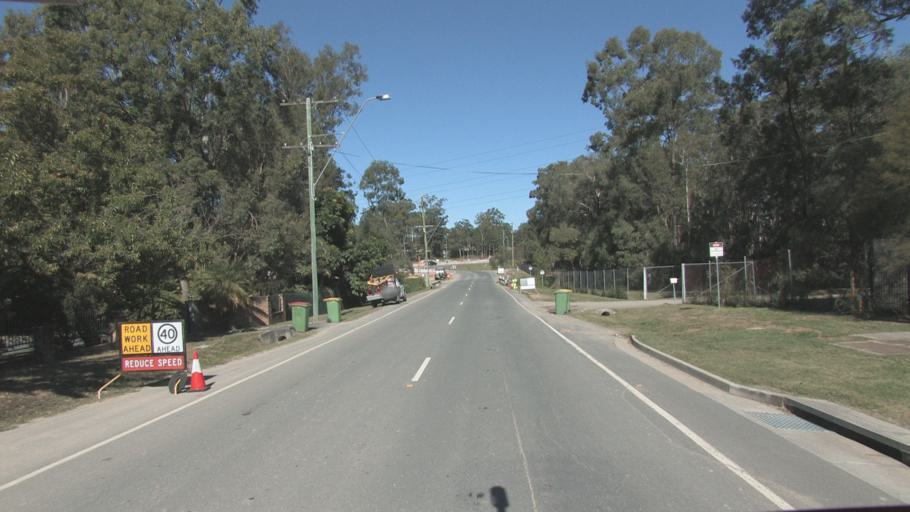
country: AU
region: Queensland
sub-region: Logan
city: Woodridge
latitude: -27.6525
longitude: 153.0682
